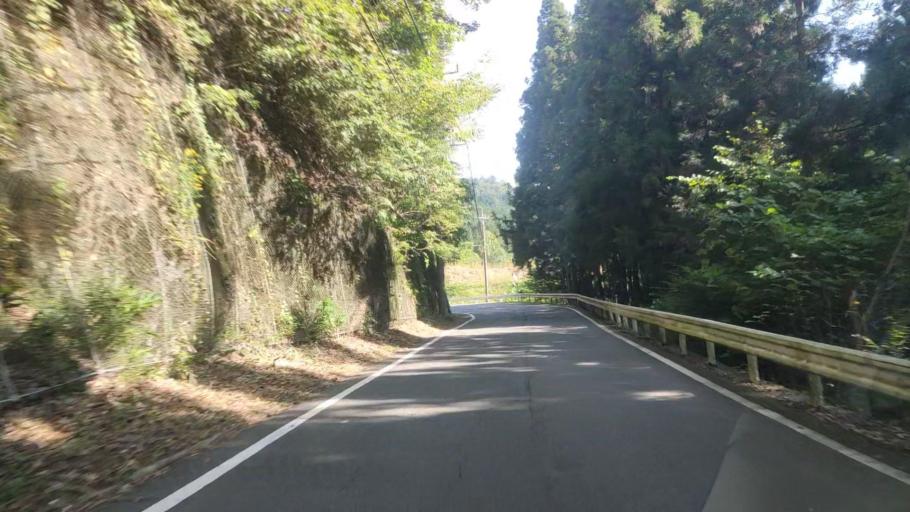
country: JP
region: Gunma
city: Nakanojomachi
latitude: 36.6024
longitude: 138.7128
